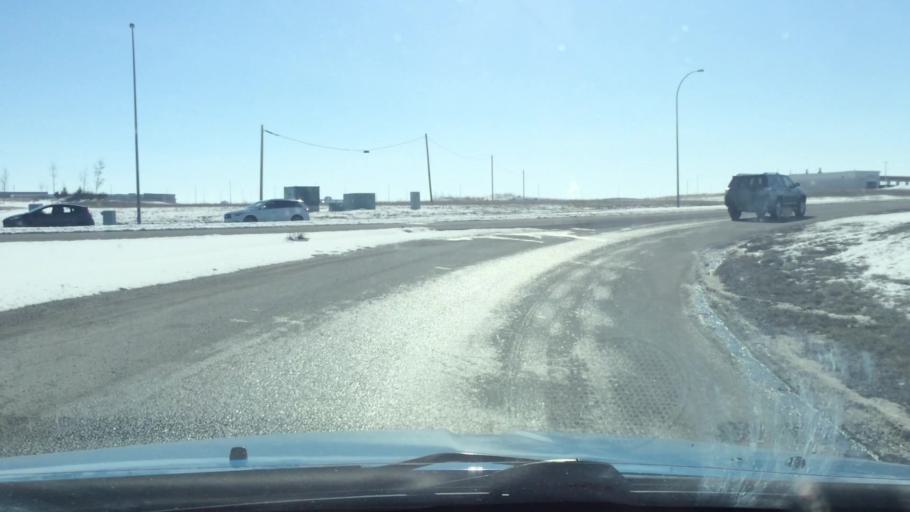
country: CA
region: Alberta
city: Airdrie
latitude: 51.2121
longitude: -113.9911
